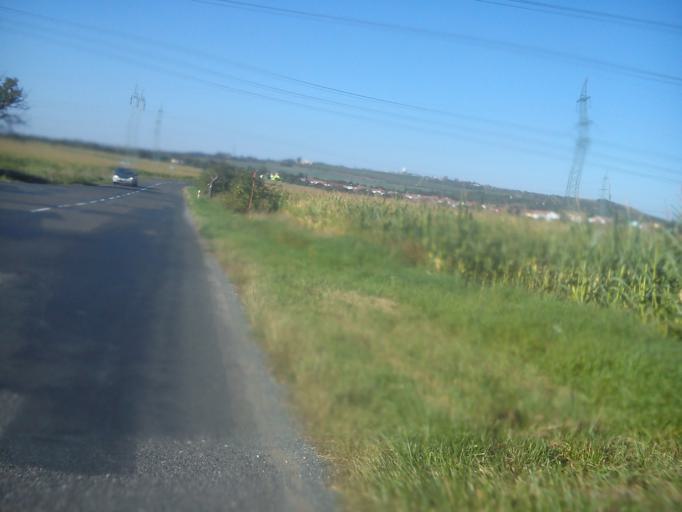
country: CZ
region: South Moravian
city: Telnice
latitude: 49.0977
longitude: 16.7420
